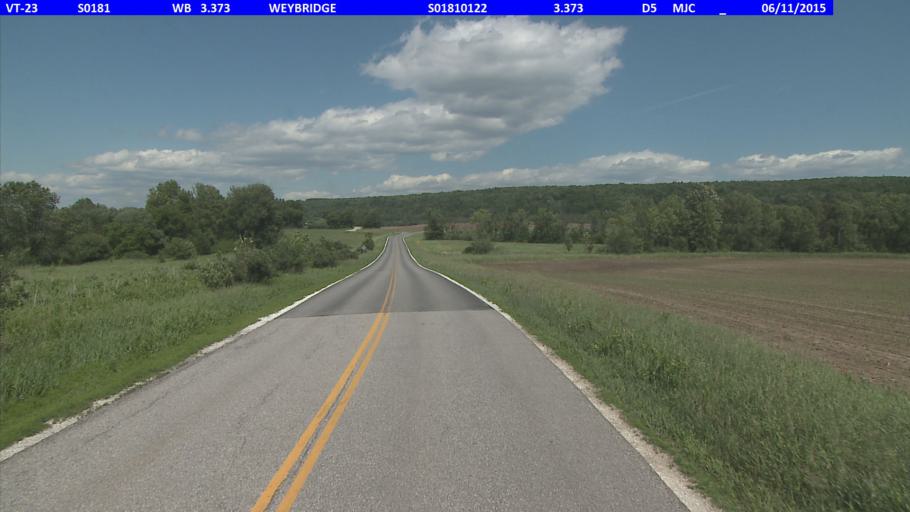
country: US
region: Vermont
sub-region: Addison County
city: Middlebury (village)
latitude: 44.0505
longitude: -73.2272
